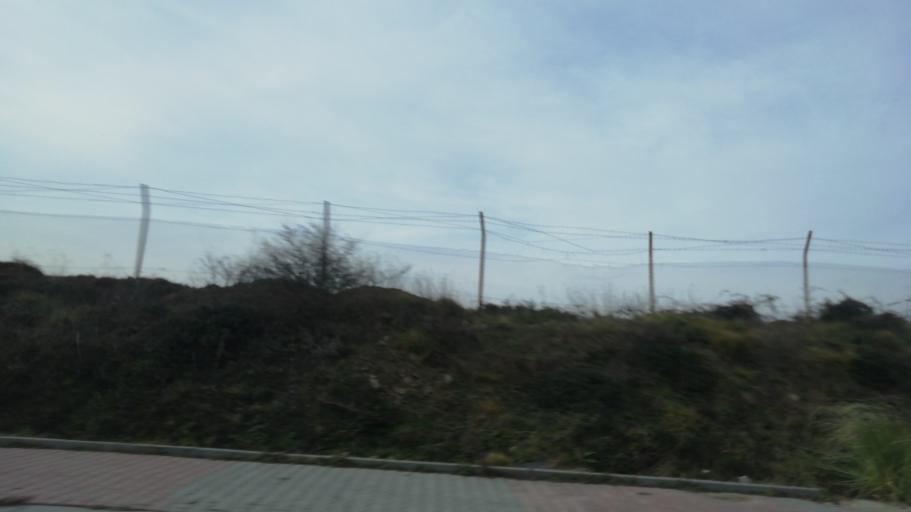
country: TR
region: Istanbul
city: Basaksehir
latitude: 41.1150
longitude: 28.7980
